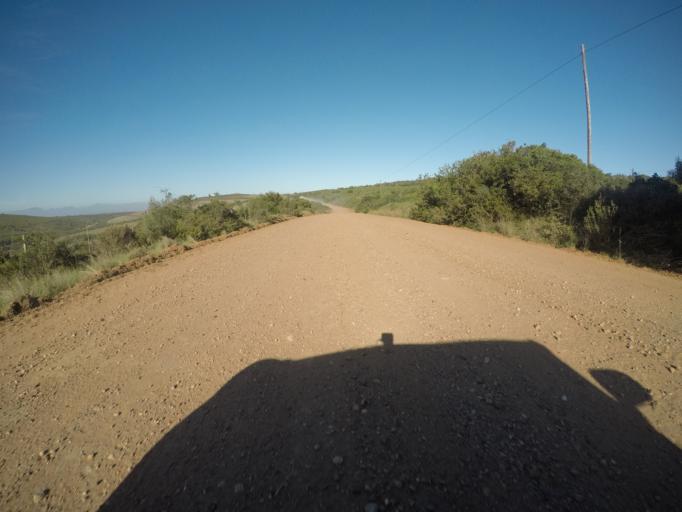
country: ZA
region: Western Cape
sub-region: Eden District Municipality
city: Mossel Bay
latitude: -34.1445
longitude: 22.0080
